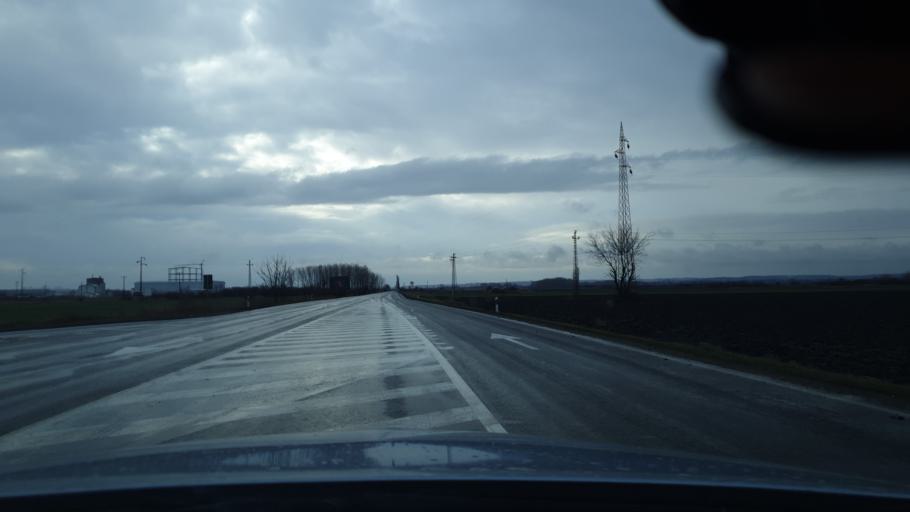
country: RS
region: Autonomna Pokrajina Vojvodina
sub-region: Juznobanatski Okrug
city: Kovin
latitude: 44.7323
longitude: 20.9653
